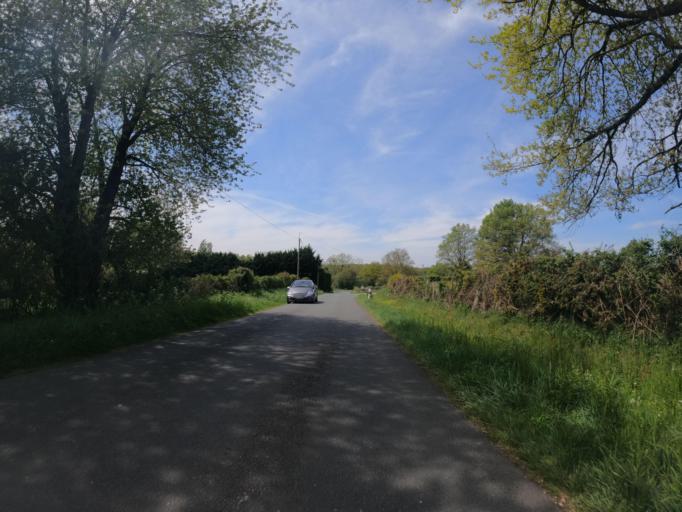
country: FR
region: Poitou-Charentes
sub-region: Departement des Deux-Sevres
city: Secondigny
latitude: 46.6426
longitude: -0.5081
